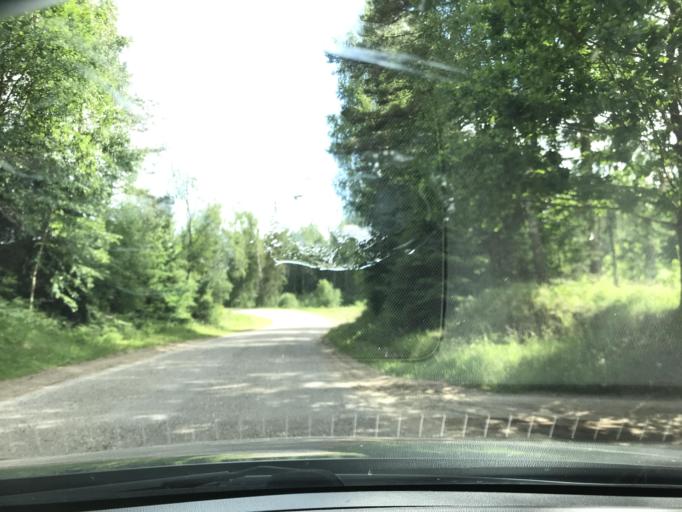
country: LV
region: Alsunga
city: Alsunga
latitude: 56.9856
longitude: 21.6304
